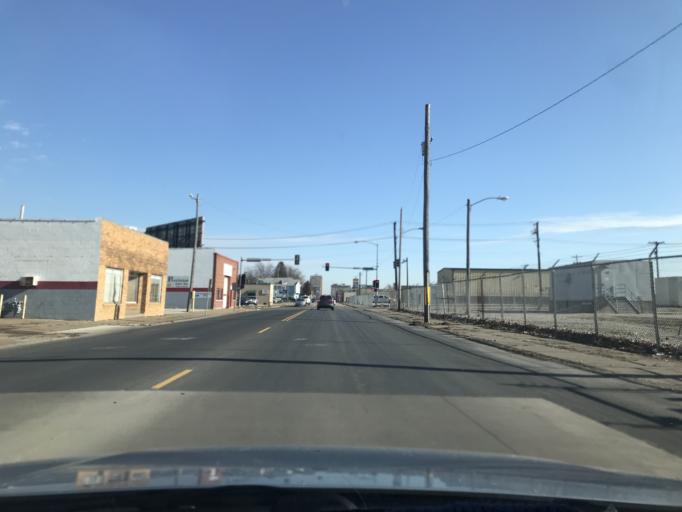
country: US
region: Iowa
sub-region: Scott County
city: Davenport
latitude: 41.5213
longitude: -90.5918
